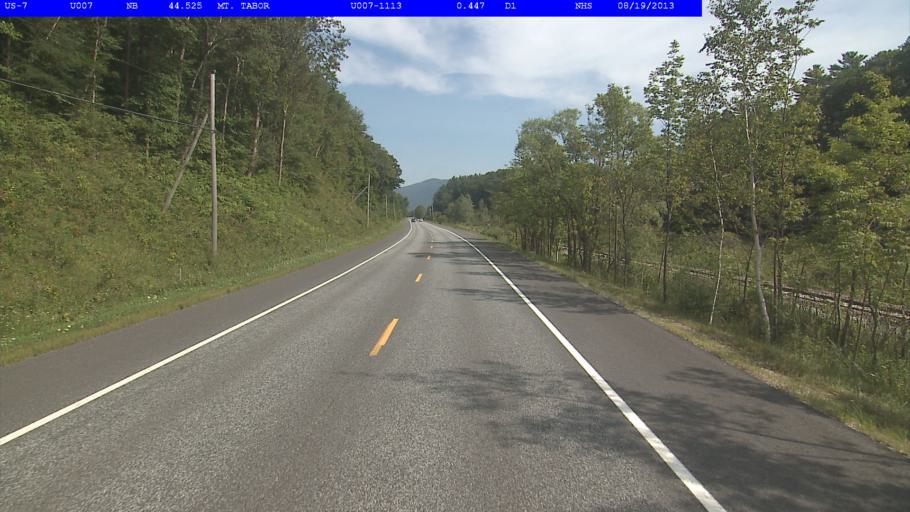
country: US
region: Vermont
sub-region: Bennington County
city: Manchester Center
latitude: 43.3114
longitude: -72.9931
